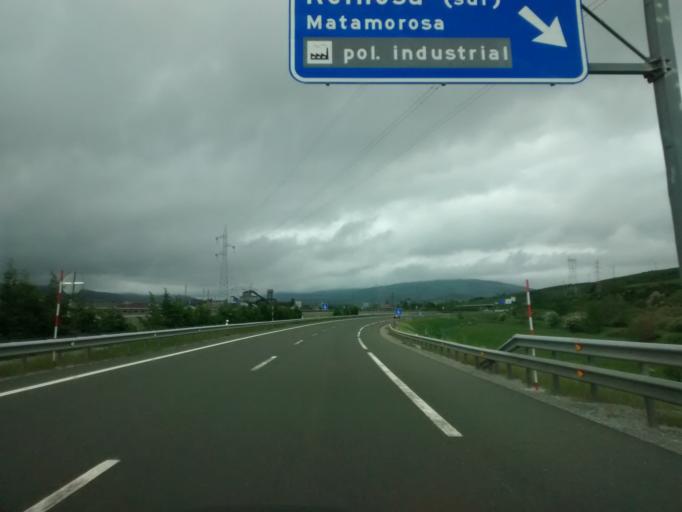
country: ES
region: Cantabria
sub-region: Provincia de Cantabria
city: Reinosa
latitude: 42.9802
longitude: -4.1445
